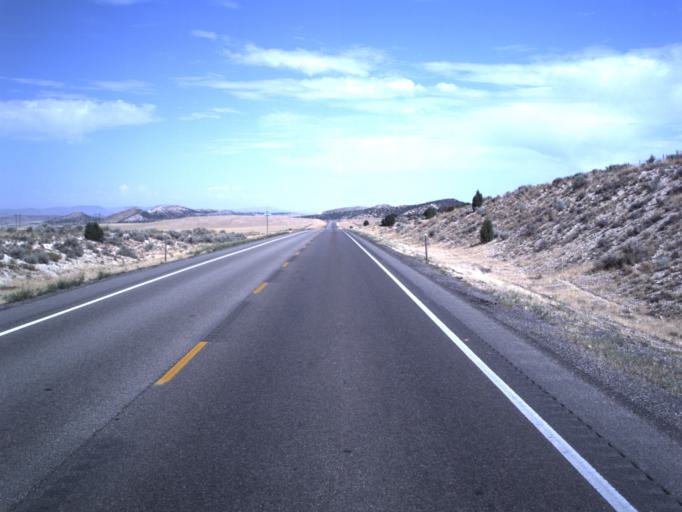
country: US
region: Utah
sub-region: Sanpete County
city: Gunnison
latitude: 39.3228
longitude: -111.9089
